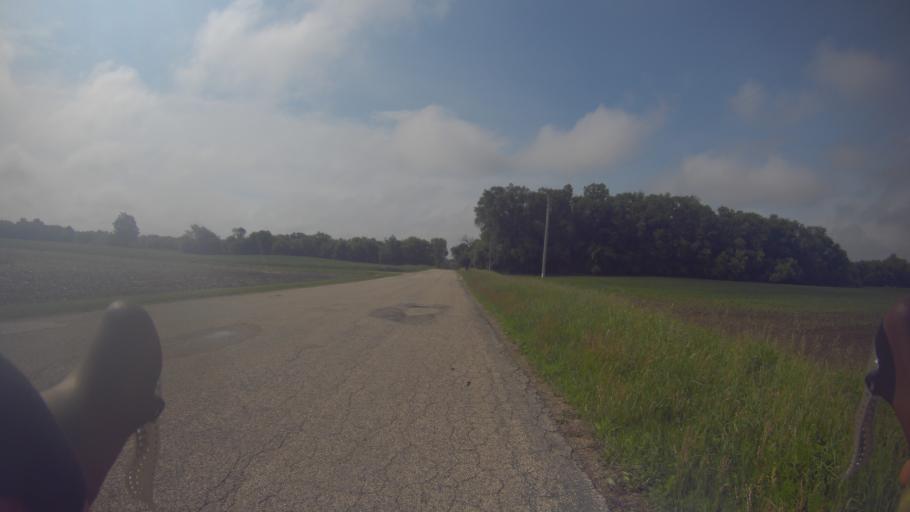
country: US
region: Wisconsin
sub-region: Dane County
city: Stoughton
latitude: 42.9504
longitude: -89.1810
